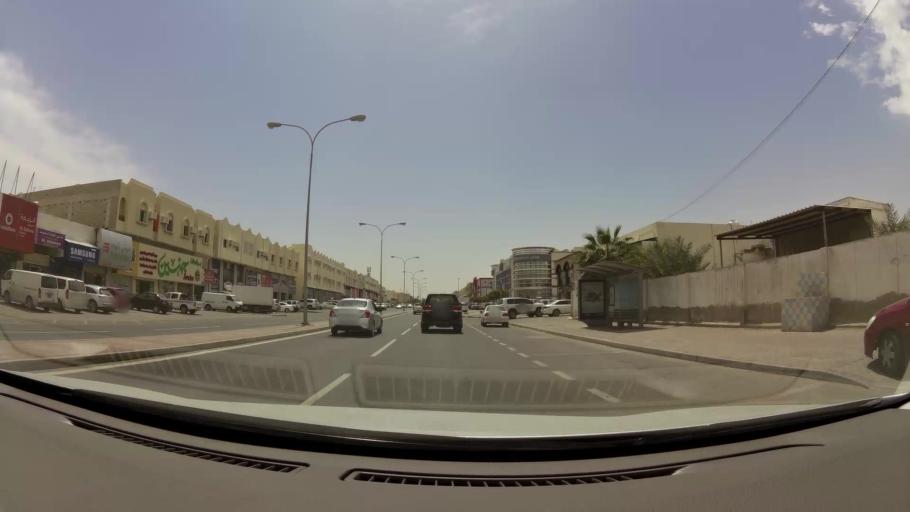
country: QA
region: Baladiyat ar Rayyan
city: Ar Rayyan
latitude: 25.2920
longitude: 51.4199
